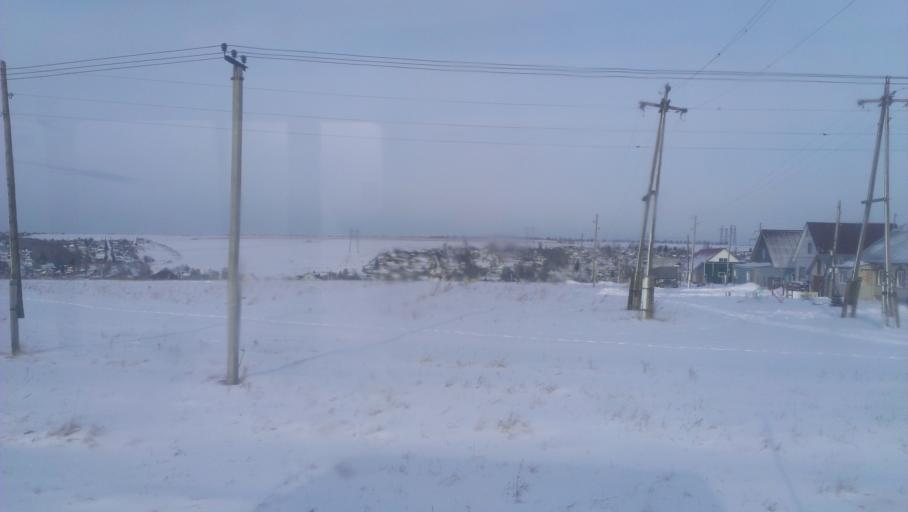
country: RU
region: Altai Krai
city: Gon'ba
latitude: 53.4122
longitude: 83.5603
